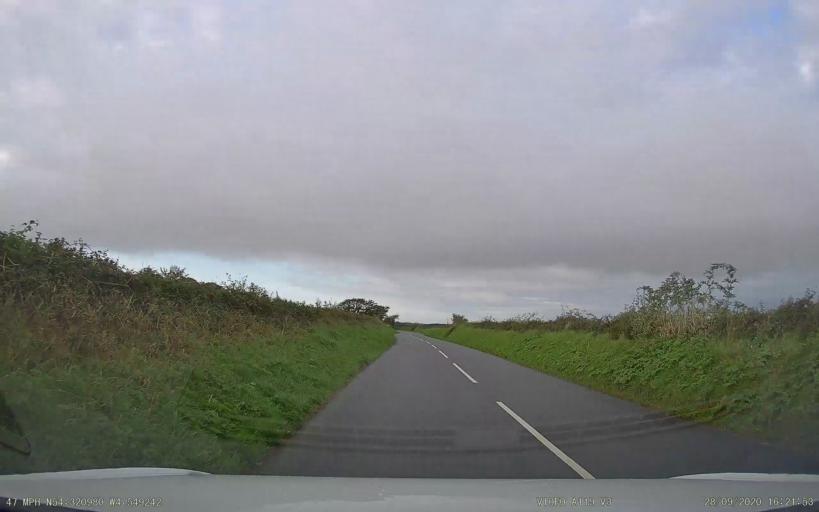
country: IM
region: Ramsey
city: Ramsey
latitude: 54.3210
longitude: -4.5492
